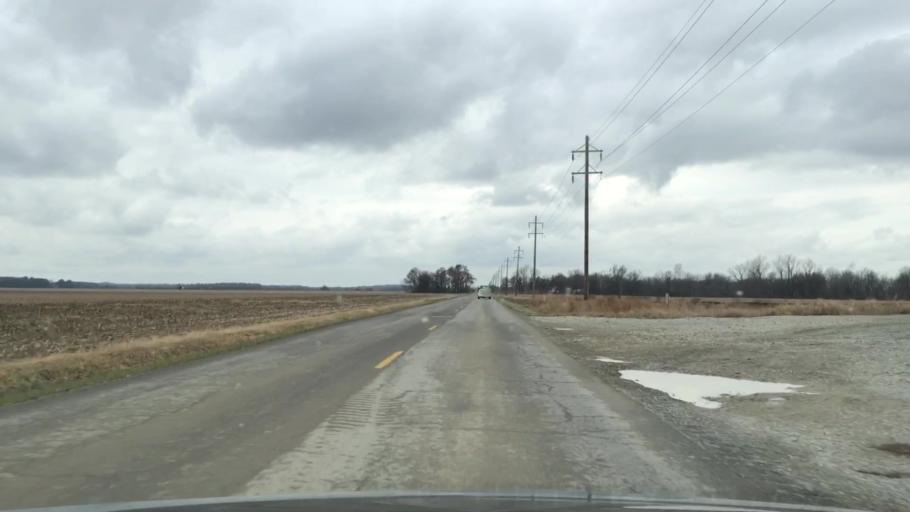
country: US
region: Kentucky
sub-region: McLean County
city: Calhoun
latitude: 37.5244
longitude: -87.2920
